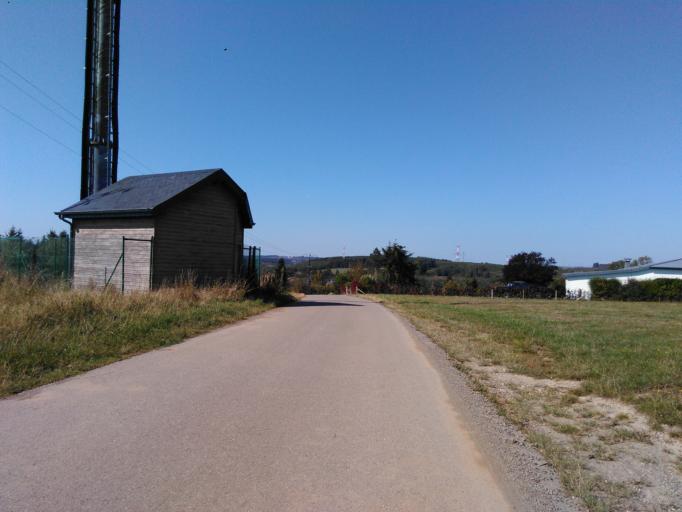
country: BE
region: Wallonia
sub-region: Province du Luxembourg
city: Martelange
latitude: 49.8296
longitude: 5.7515
